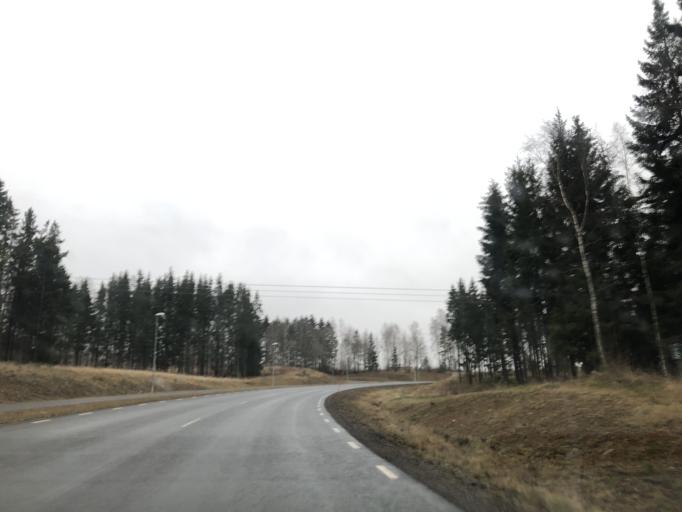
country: SE
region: Vaestra Goetaland
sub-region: Ulricehamns Kommun
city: Ulricehamn
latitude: 57.8159
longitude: 13.2887
